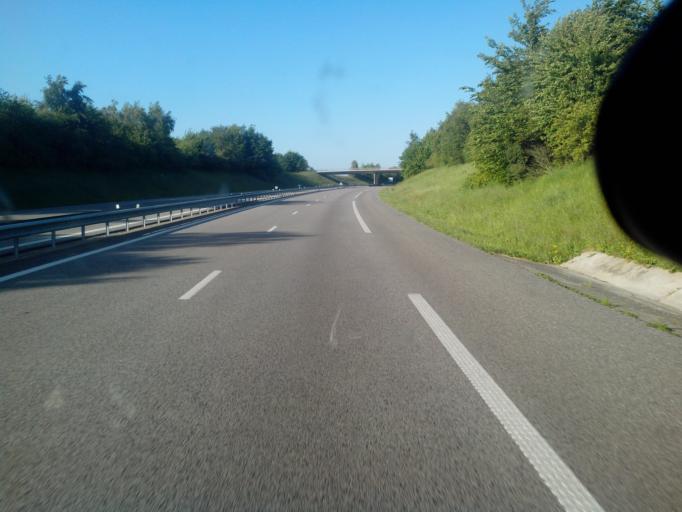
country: FR
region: Haute-Normandie
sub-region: Departement de la Seine-Maritime
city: Etainhus
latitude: 49.5657
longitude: 0.3436
